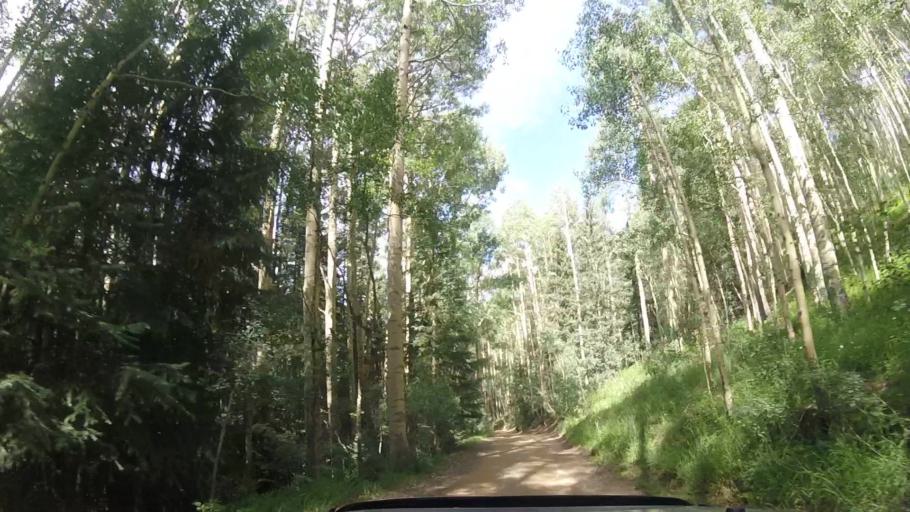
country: US
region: Colorado
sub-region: San Miguel County
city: Telluride
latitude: 37.8575
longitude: -107.8182
